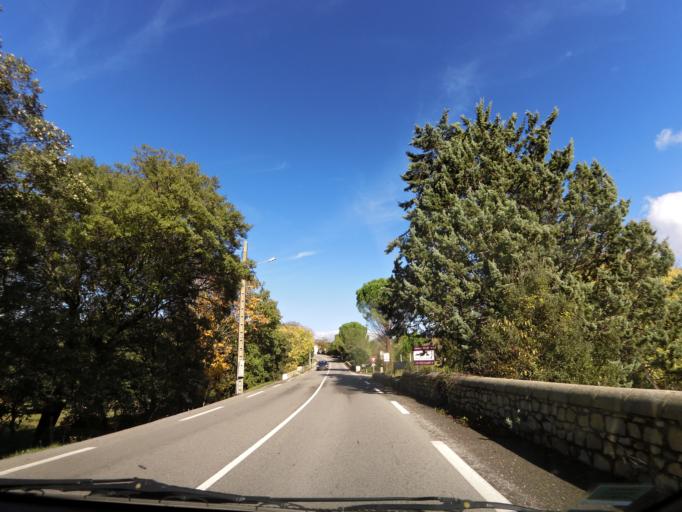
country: FR
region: Languedoc-Roussillon
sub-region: Departement du Gard
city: Villevieille
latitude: 43.8786
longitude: 4.0958
